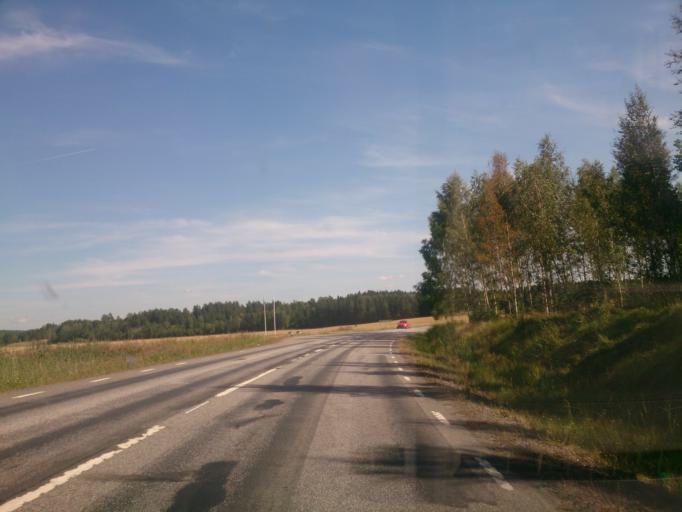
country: SE
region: OEstergoetland
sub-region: Norrkopings Kommun
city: Norrkoping
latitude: 58.4938
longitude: 16.1263
